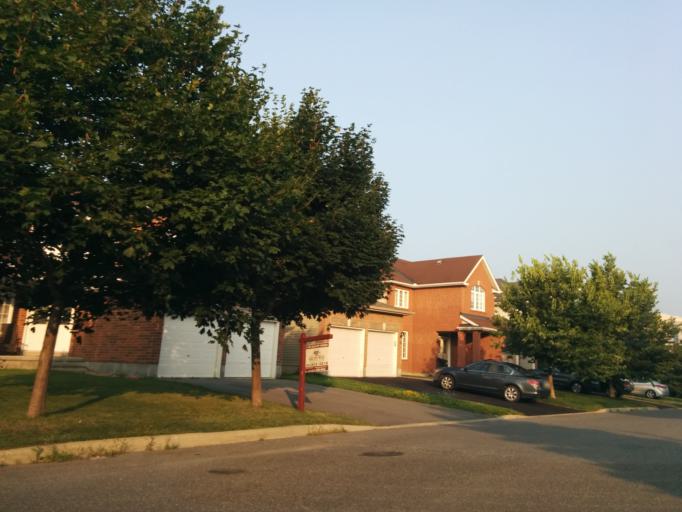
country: CA
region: Ontario
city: Ottawa
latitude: 45.3684
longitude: -75.7398
